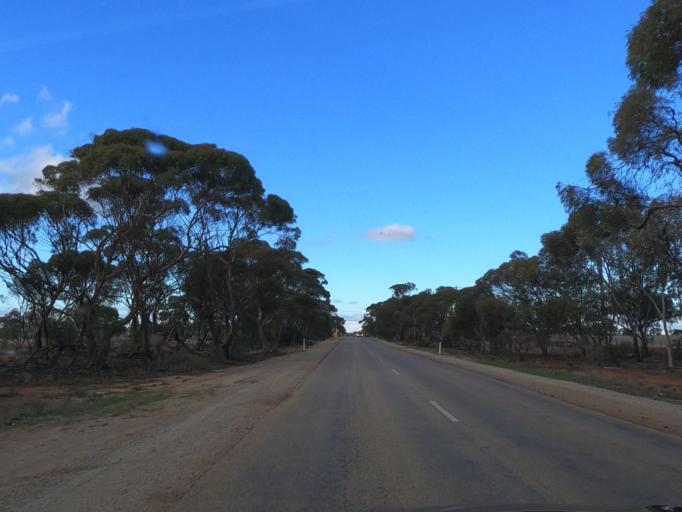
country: AU
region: Victoria
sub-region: Swan Hill
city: Swan Hill
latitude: -35.3470
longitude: 143.5197
